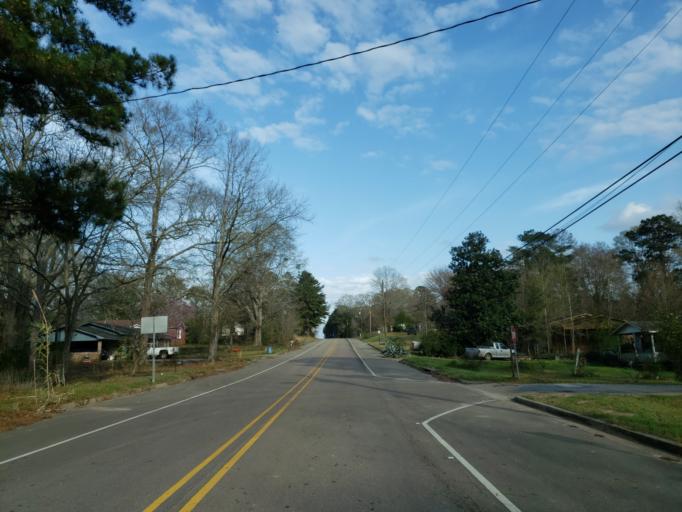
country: US
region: Mississippi
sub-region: Jones County
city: Sharon
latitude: 31.7880
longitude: -89.0443
